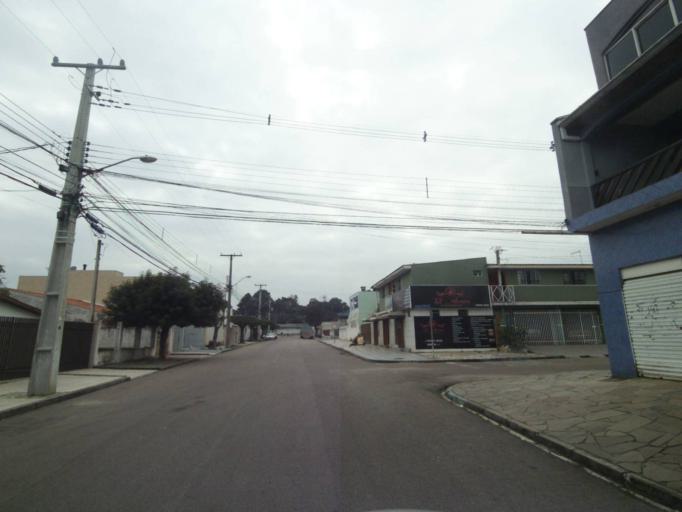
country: BR
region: Parana
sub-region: Curitiba
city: Curitiba
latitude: -25.5140
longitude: -49.3252
